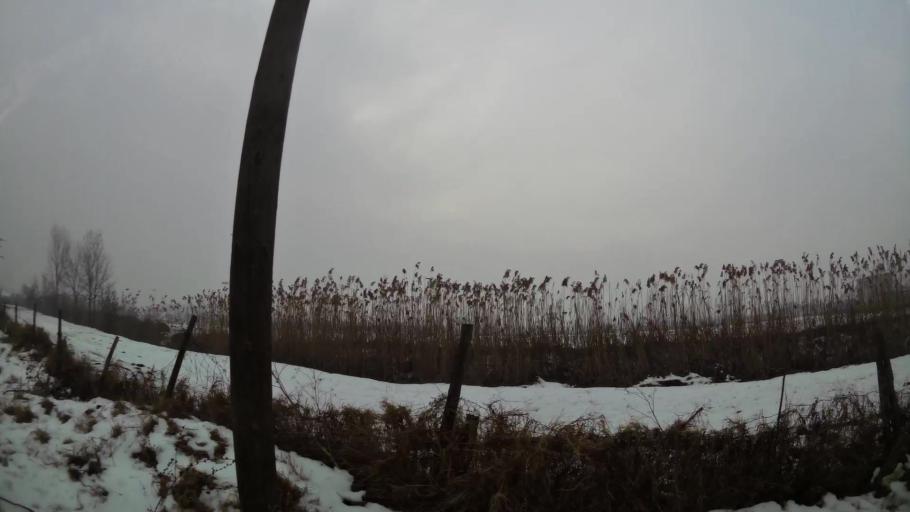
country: MK
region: Petrovec
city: Petrovec
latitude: 41.9349
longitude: 21.6126
